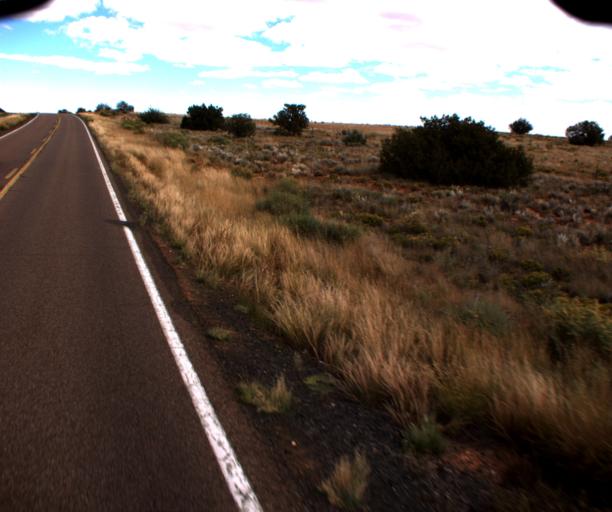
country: US
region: Arizona
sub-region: Navajo County
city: Snowflake
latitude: 34.6466
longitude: -110.3484
